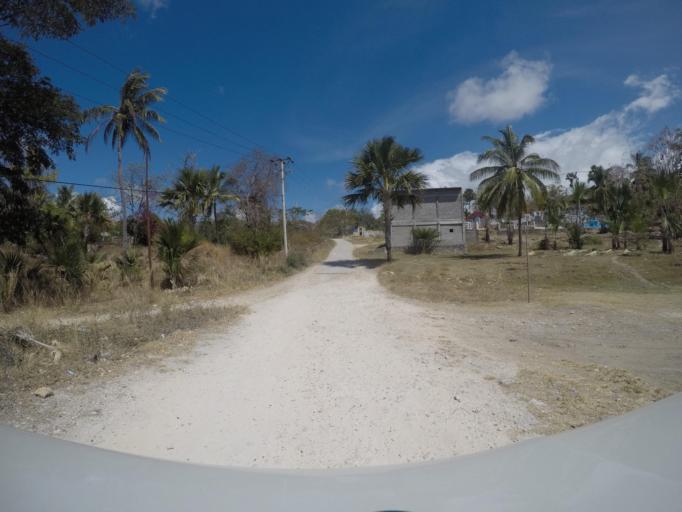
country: TL
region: Baucau
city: Baucau
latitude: -8.4544
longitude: 126.4418
